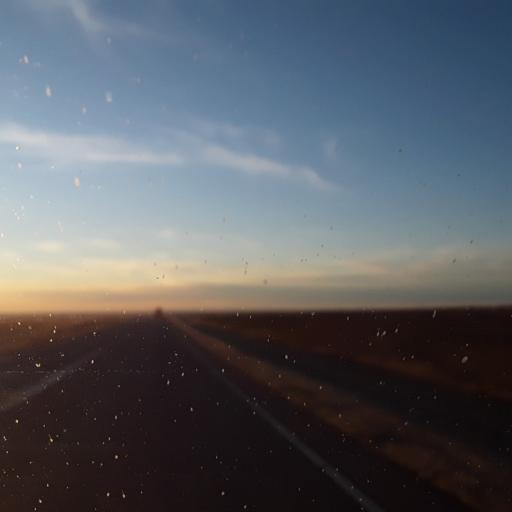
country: US
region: Colorado
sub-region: Cheyenne County
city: Cheyenne Wells
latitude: 38.8153
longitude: -102.5586
